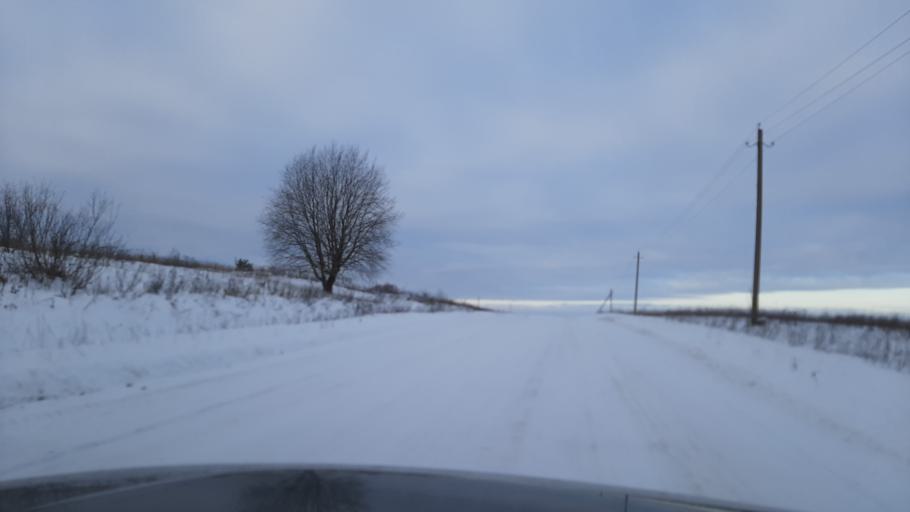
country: RU
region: Kostroma
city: Volgorechensk
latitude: 57.4439
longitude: 40.9367
